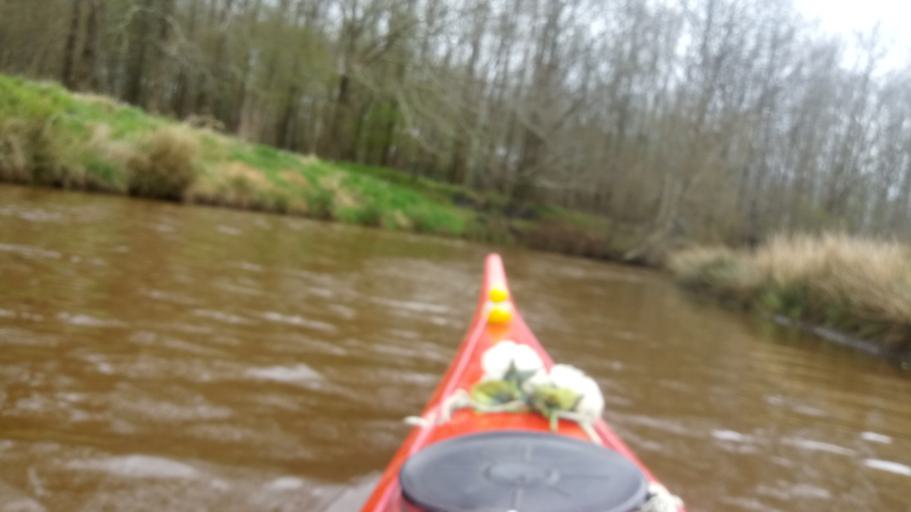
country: NL
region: Groningen
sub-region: Gemeente Vlagtwedde
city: Sellingen
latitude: 52.9631
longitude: 7.1414
